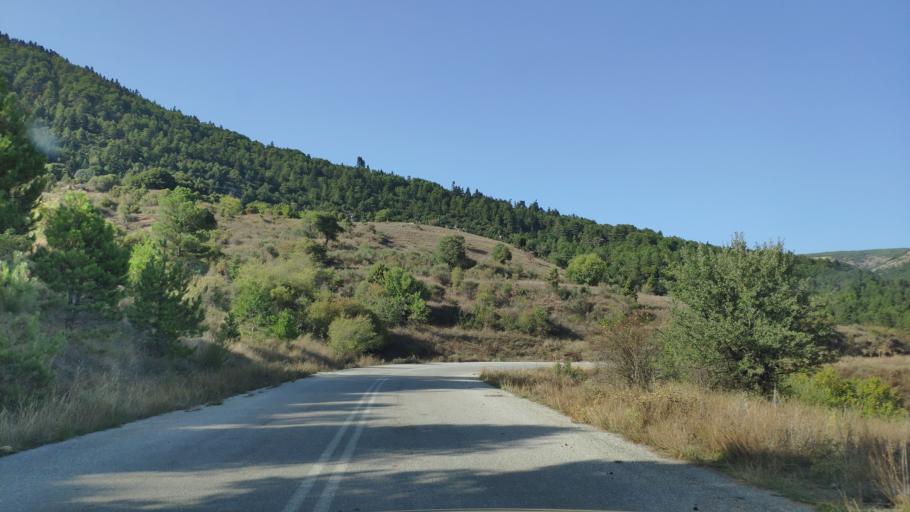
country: GR
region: West Greece
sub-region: Nomos Achaias
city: Aiyira
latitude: 38.0083
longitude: 22.4009
